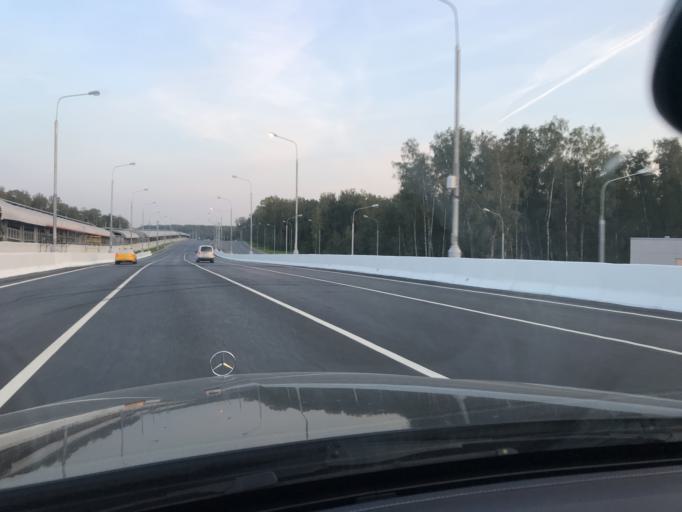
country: RU
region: Moscow
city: Solntsevo
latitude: 55.5971
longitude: 37.4147
